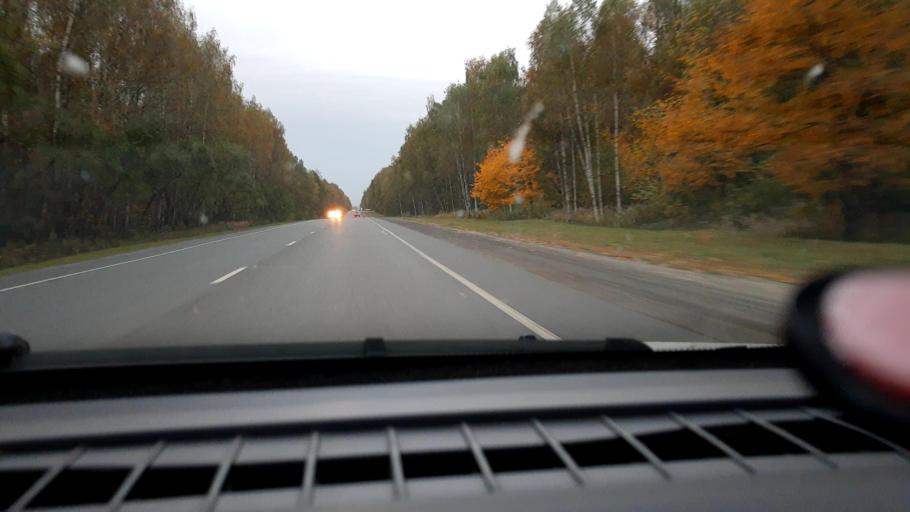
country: RU
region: Vladimir
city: Orgtrud
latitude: 56.2099
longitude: 40.6394
